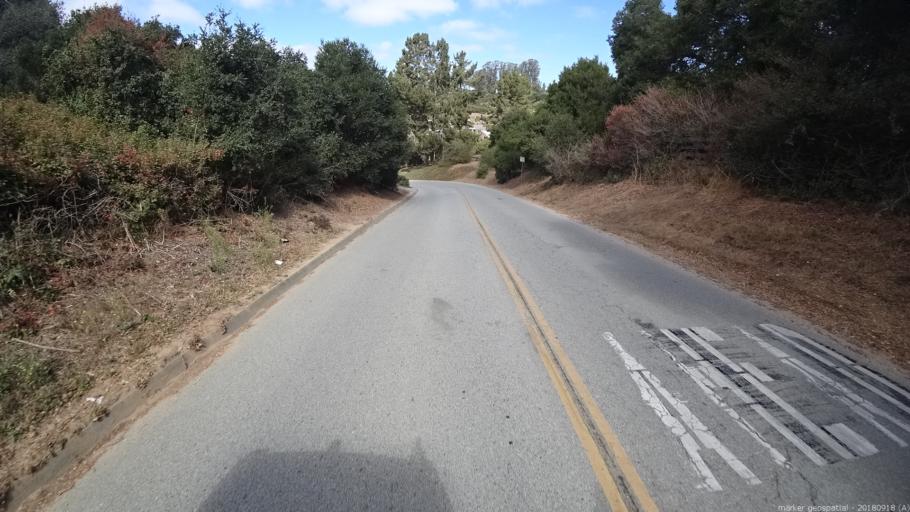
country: US
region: California
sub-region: Monterey County
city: Prunedale
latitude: 36.7922
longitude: -121.6612
